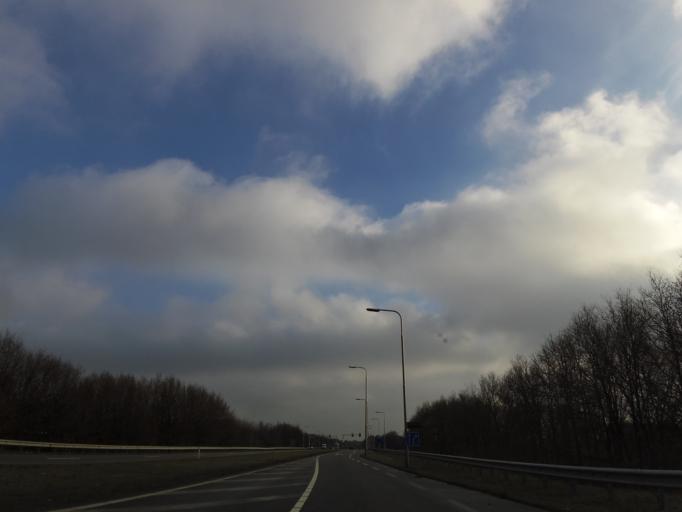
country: NL
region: Limburg
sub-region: Gemeente Gennep
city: Gennep
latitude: 51.6862
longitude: 5.9730
